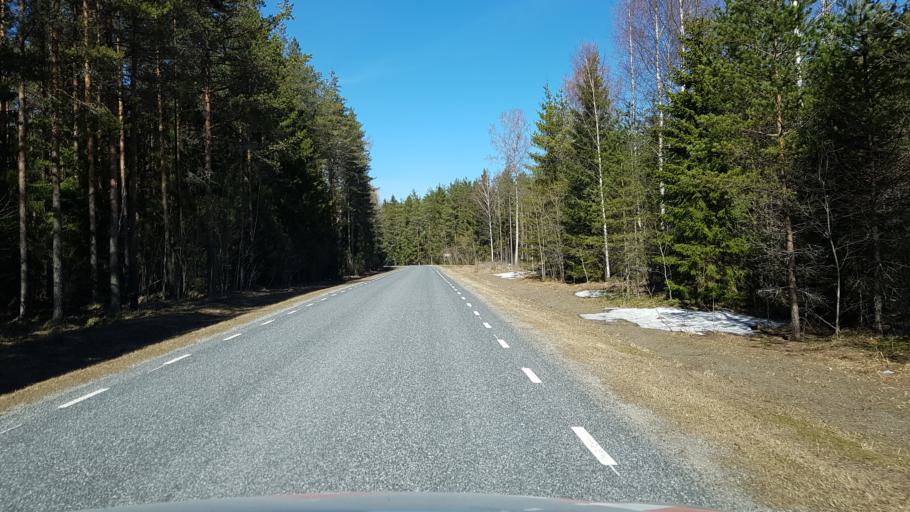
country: EE
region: Laeaene-Virumaa
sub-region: Vinni vald
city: Vinni
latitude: 59.1377
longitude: 26.5250
